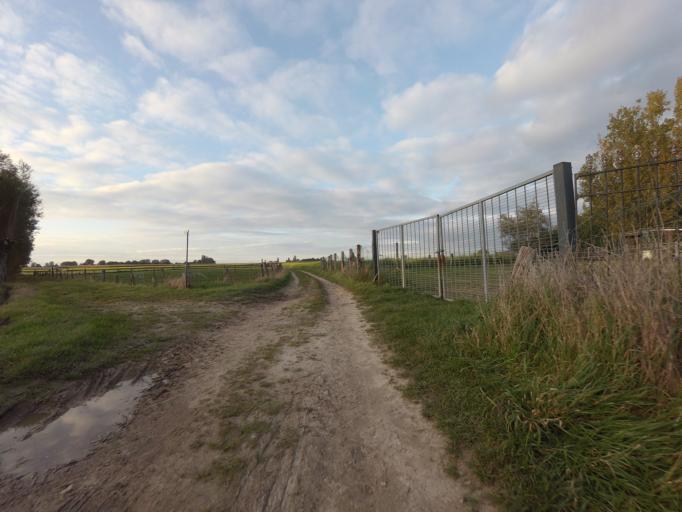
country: BE
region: Flanders
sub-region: Provincie Vlaams-Brabant
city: Grimbergen
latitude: 50.9406
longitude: 4.3534
